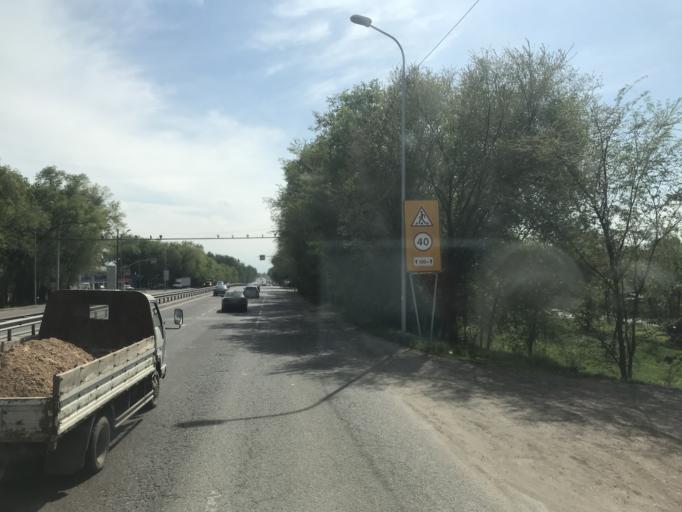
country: KZ
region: Almaty Oblysy
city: Pervomayskiy
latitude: 43.3360
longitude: 76.9157
